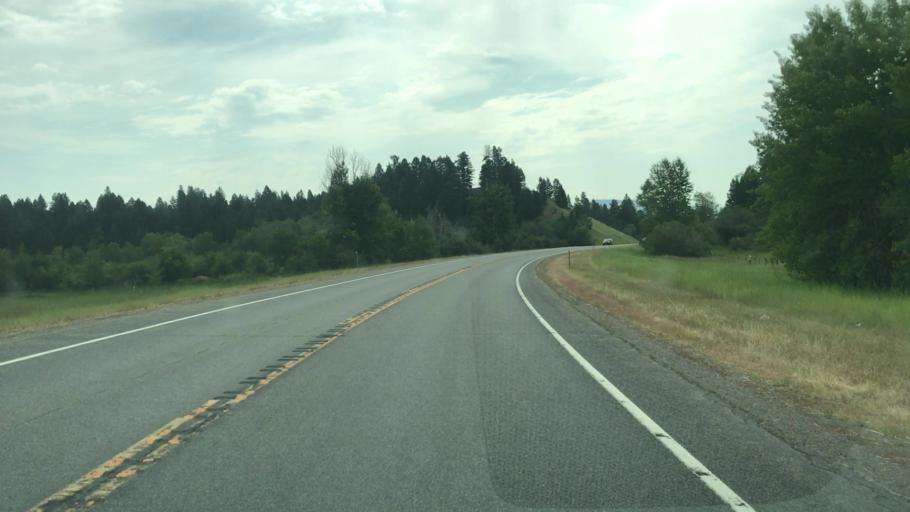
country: US
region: Montana
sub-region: Lewis and Clark County
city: Lincoln
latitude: 47.0160
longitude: -113.0723
